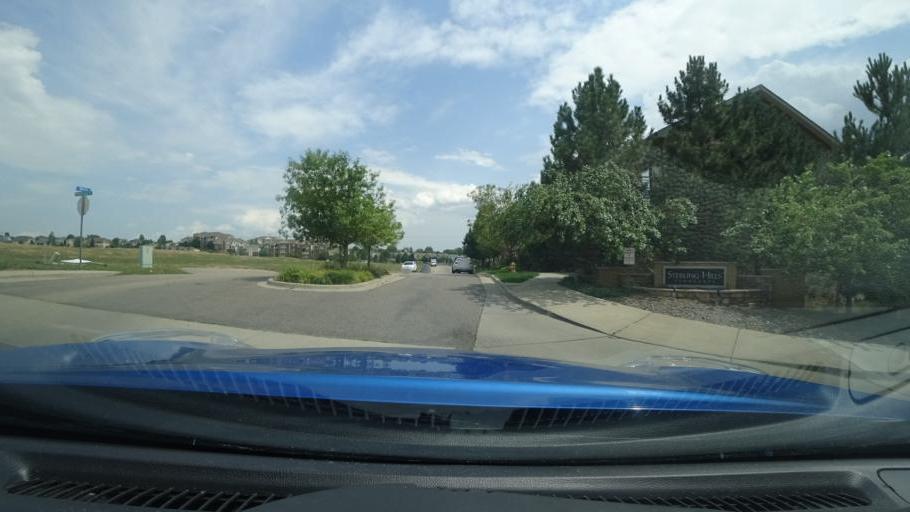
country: US
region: Colorado
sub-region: Adams County
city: Aurora
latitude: 39.6695
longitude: -104.7684
